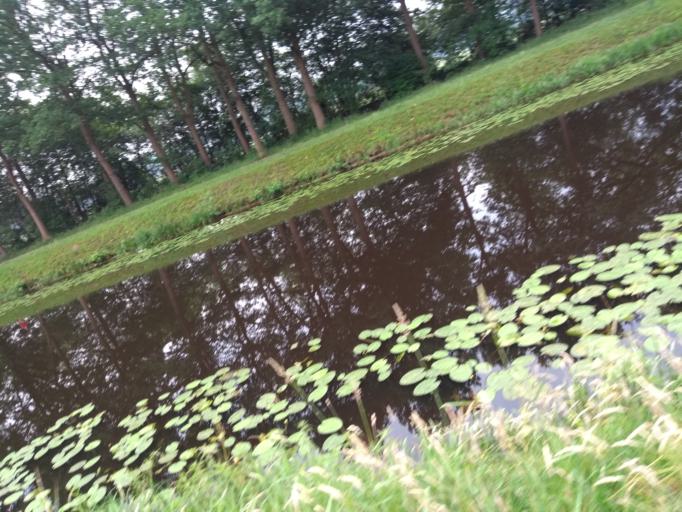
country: NL
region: Overijssel
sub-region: Gemeente Almelo
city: Almelo
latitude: 52.3679
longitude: 6.6963
